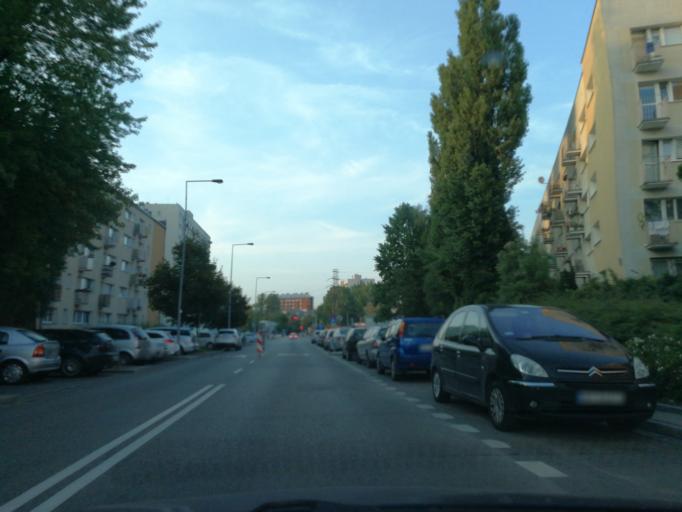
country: PL
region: Masovian Voivodeship
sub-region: Warszawa
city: Zoliborz
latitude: 52.2651
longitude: 20.9621
